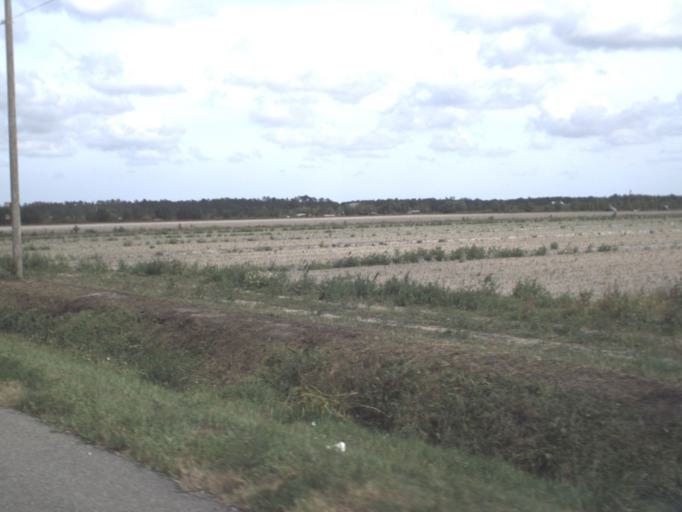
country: US
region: Florida
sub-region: Flagler County
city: Bunnell
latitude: 29.4821
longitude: -81.3623
